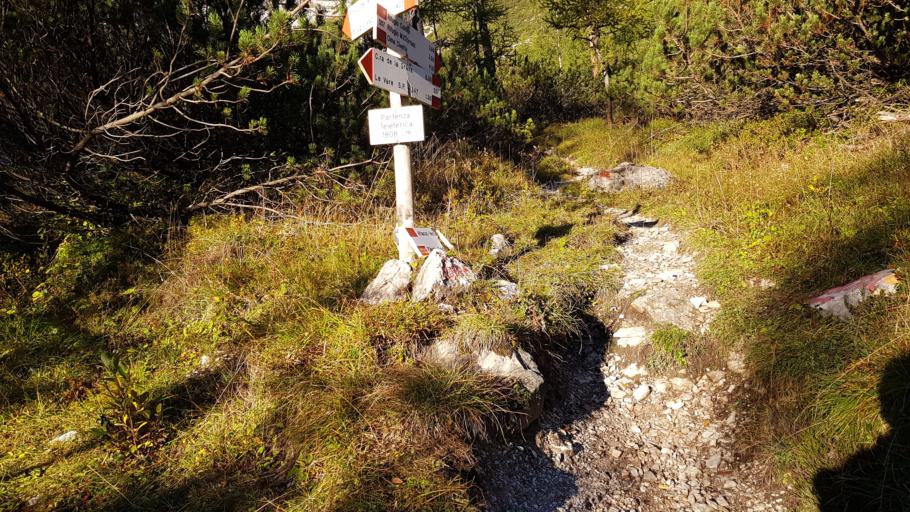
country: IT
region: Veneto
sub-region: Provincia di Belluno
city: Fusine
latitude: 46.3702
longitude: 12.0809
